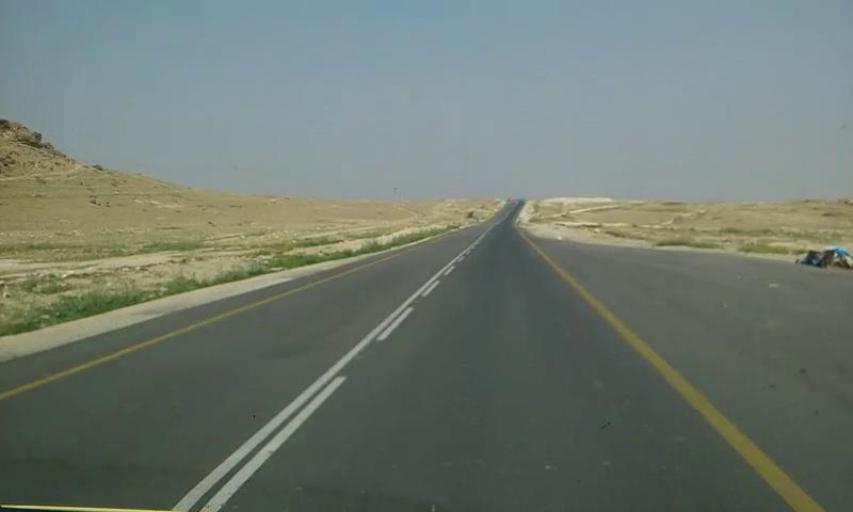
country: PS
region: West Bank
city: Al `Awja
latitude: 31.9679
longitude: 35.4703
